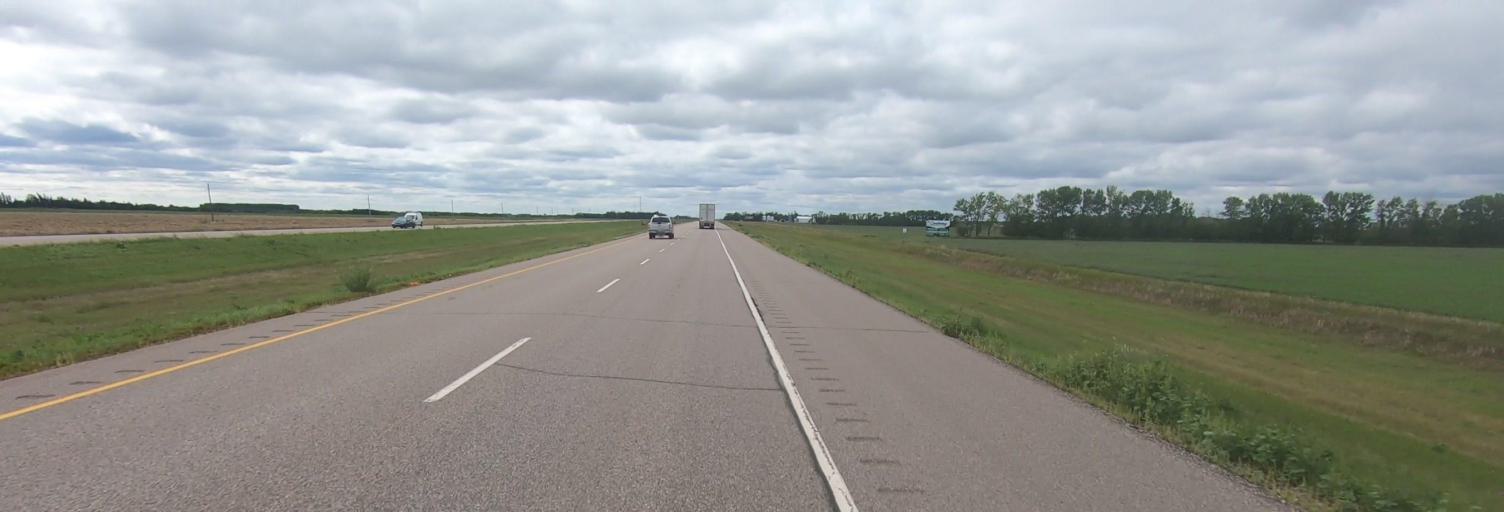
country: CA
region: Manitoba
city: Carberry
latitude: 49.9016
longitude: -99.3031
